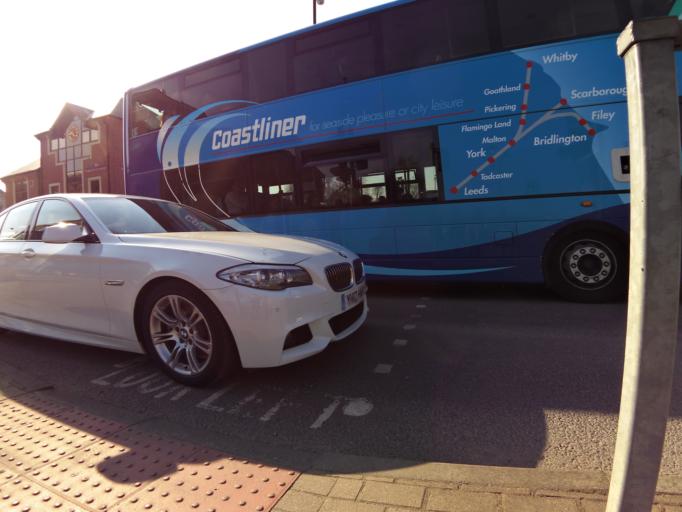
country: GB
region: England
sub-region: City of York
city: York
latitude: 53.9612
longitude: -1.0742
